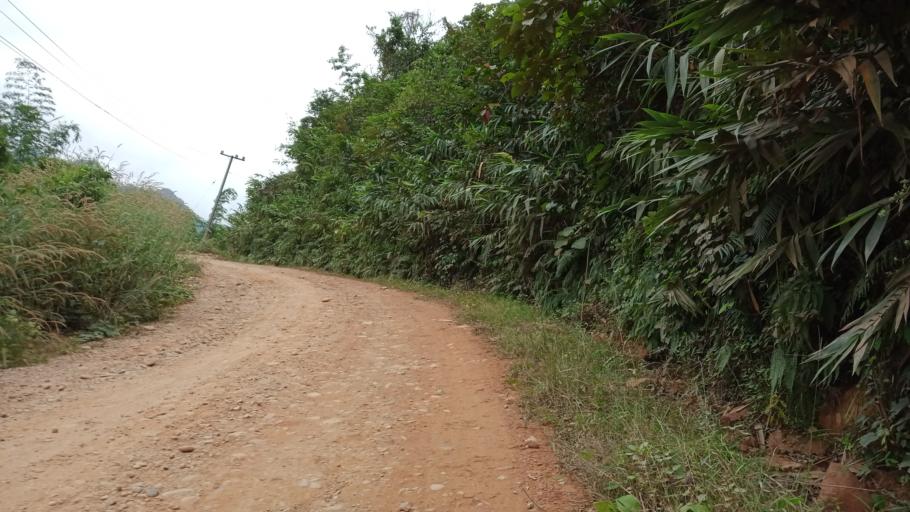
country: LA
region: Xiangkhoang
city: Phonsavan
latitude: 19.0946
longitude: 102.9902
